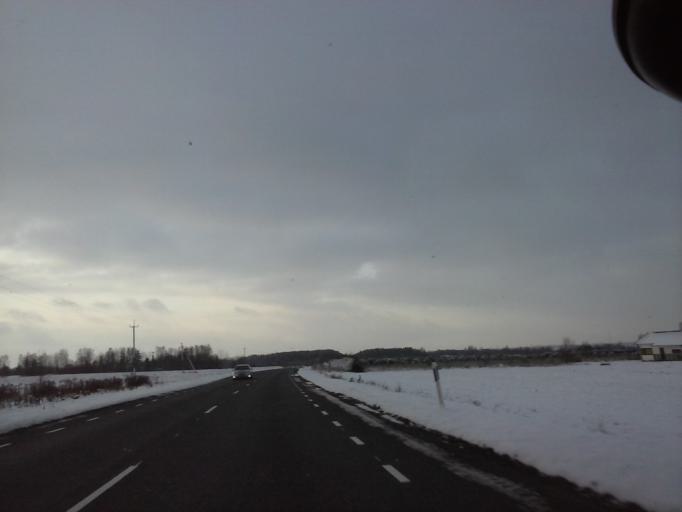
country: EE
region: Tartu
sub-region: UElenurme vald
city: Ulenurme
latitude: 58.3237
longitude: 26.8008
